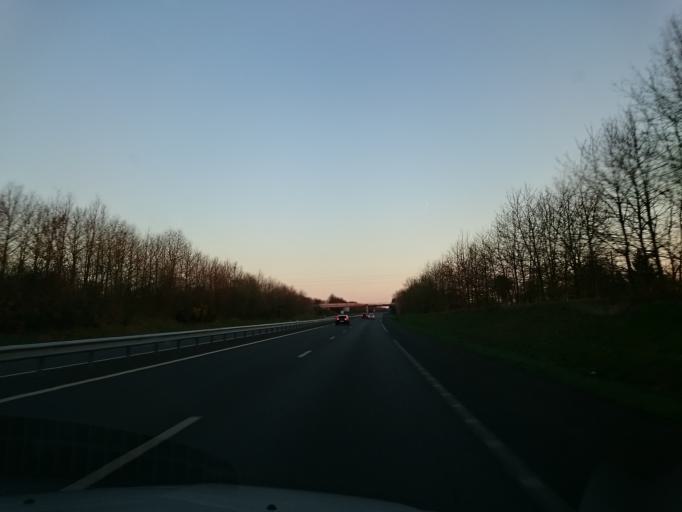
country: FR
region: Brittany
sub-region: Departement d'Ille-et-Vilaine
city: Saint-Etienne-en-Cogles
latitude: 48.3836
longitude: -1.3049
